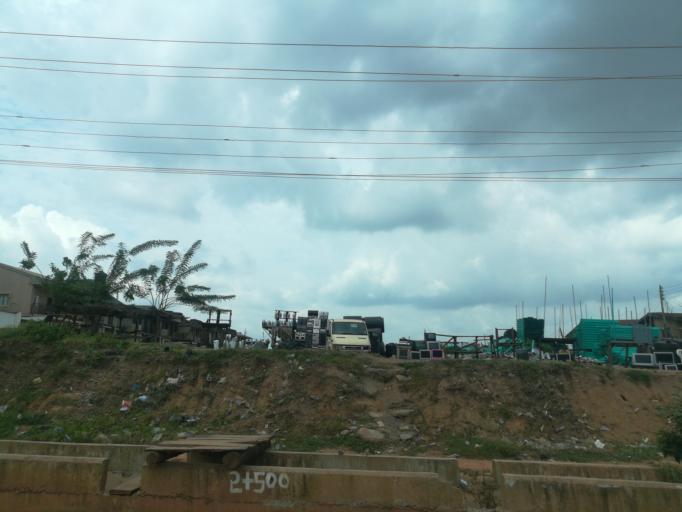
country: NG
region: Oyo
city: Ibadan
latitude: 7.4034
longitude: 3.9366
